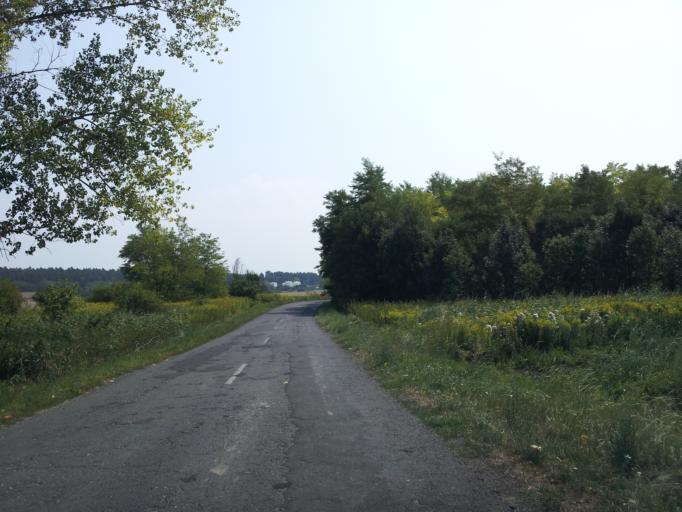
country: HU
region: Gyor-Moson-Sopron
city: Pannonhalma
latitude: 47.5103
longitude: 17.7735
